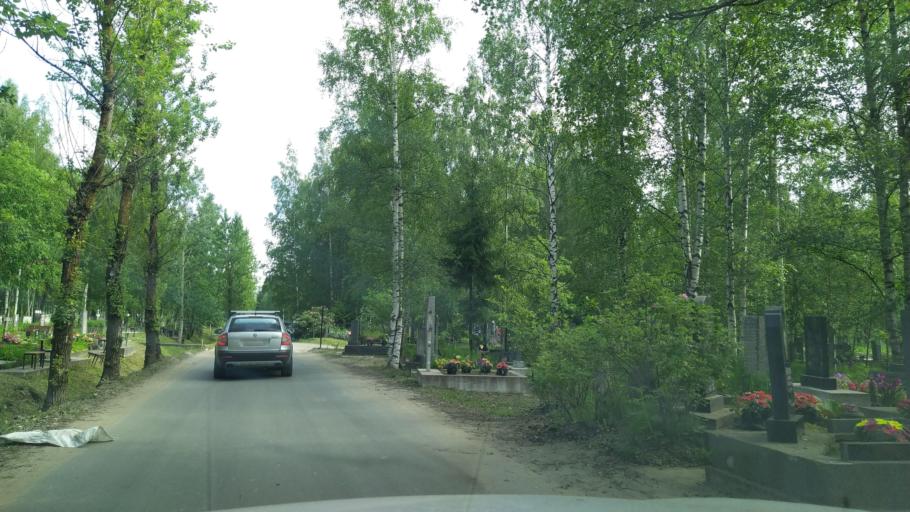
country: RU
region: St.-Petersburg
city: Dachnoye
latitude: 59.7663
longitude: 30.2622
